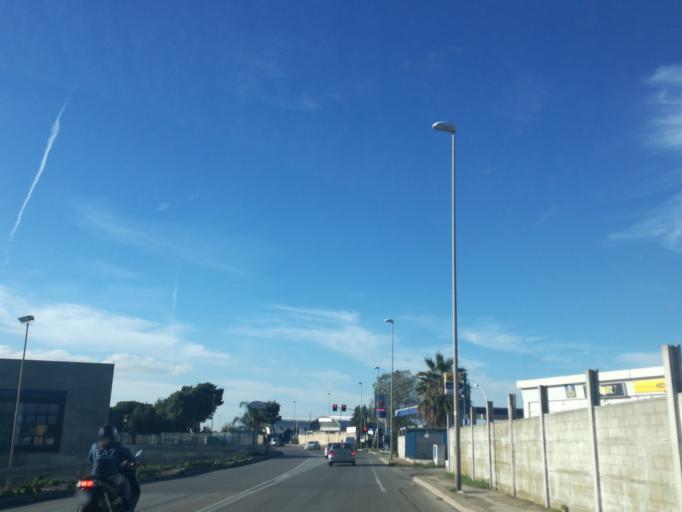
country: IT
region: Apulia
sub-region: Provincia di Bari
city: Bari
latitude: 41.1228
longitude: 16.8344
